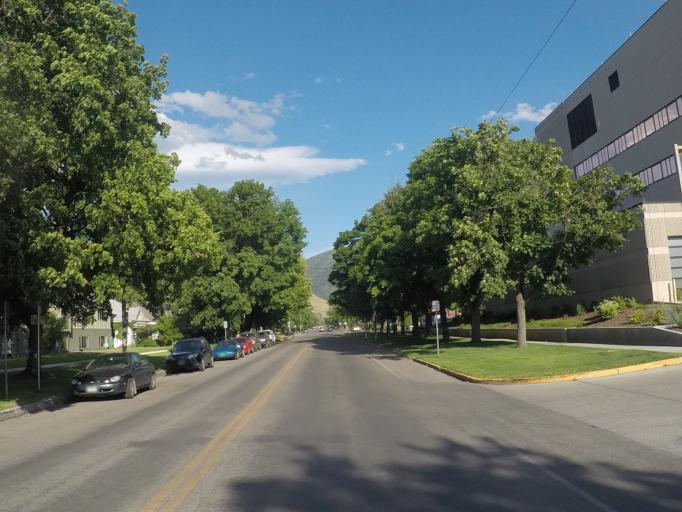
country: US
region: Montana
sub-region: Missoula County
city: Missoula
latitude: 46.8763
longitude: -114.0004
